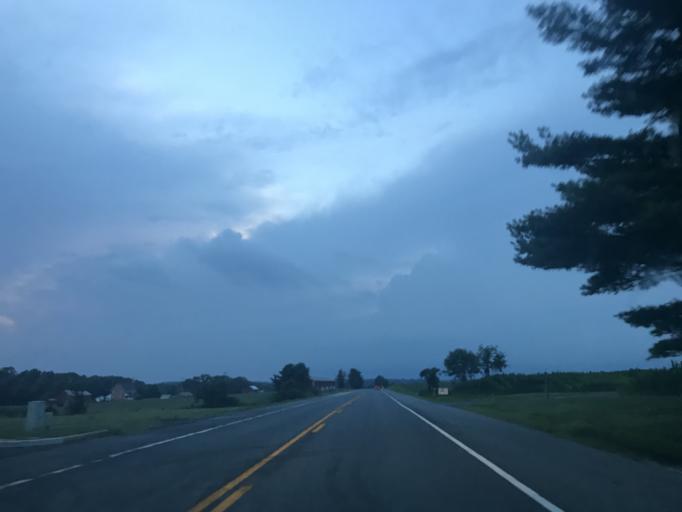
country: US
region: Maryland
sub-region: Cecil County
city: Rising Sun
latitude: 39.6881
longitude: -76.0773
